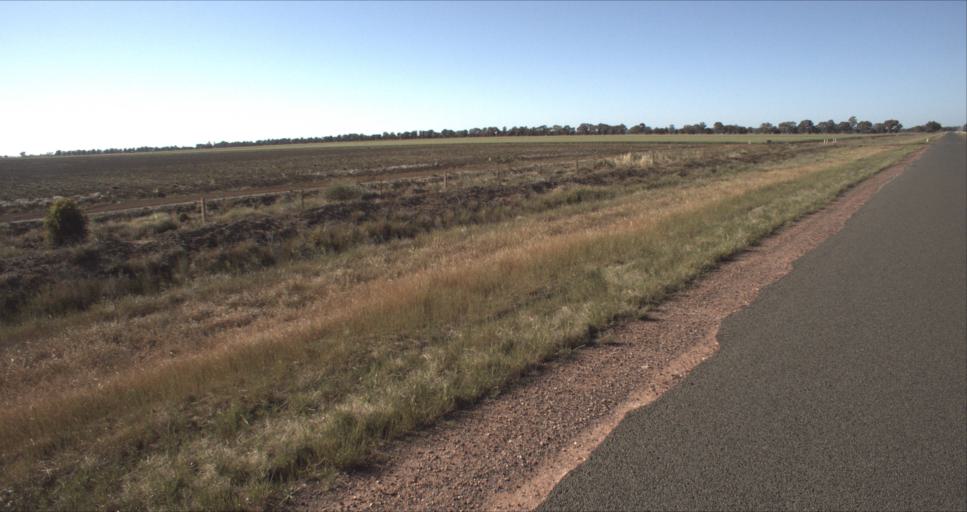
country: AU
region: New South Wales
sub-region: Leeton
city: Leeton
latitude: -34.5711
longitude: 146.2635
